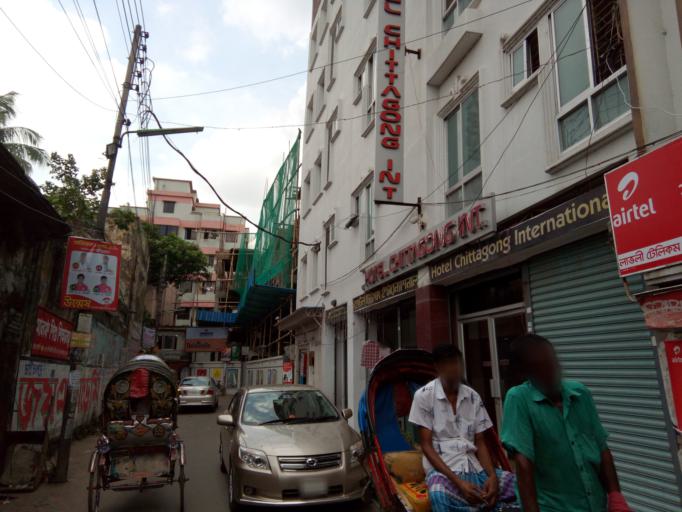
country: BD
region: Dhaka
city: Paltan
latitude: 23.7318
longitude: 90.4237
